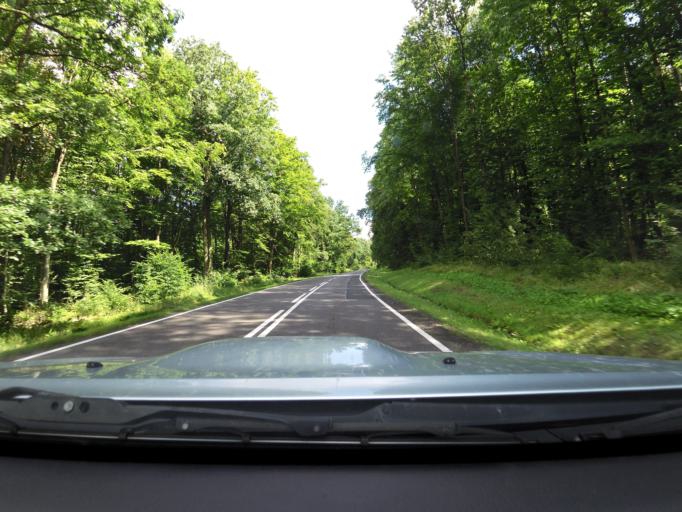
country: PL
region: Pomeranian Voivodeship
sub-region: Powiat kwidzynski
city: Ryjewo
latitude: 53.8102
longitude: 18.9688
